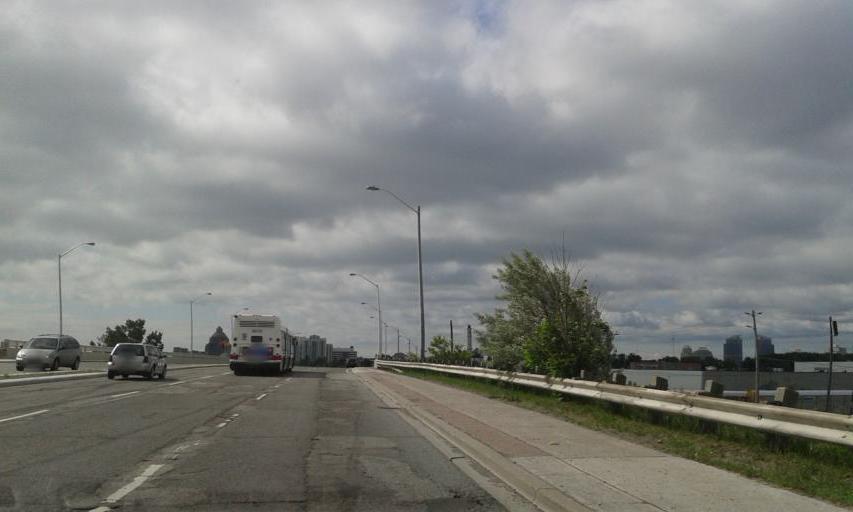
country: CA
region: Ontario
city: Scarborough
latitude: 43.8038
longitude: -79.2428
